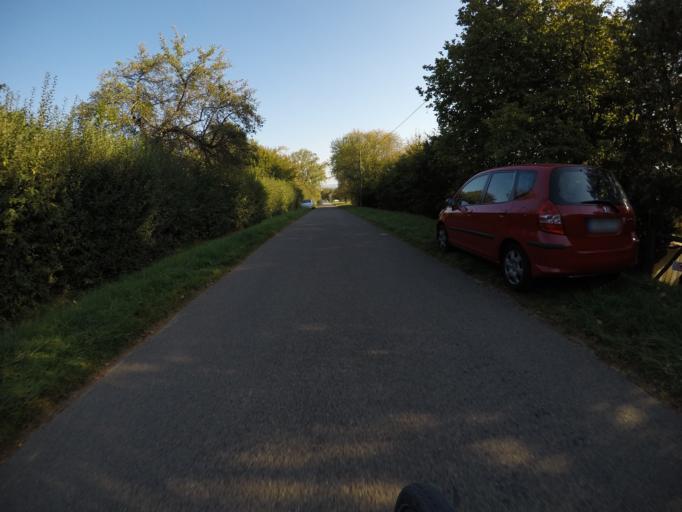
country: DE
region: Baden-Wuerttemberg
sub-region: Regierungsbezirk Stuttgart
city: Leinfelden-Echterdingen
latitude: 48.7187
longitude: 9.1946
